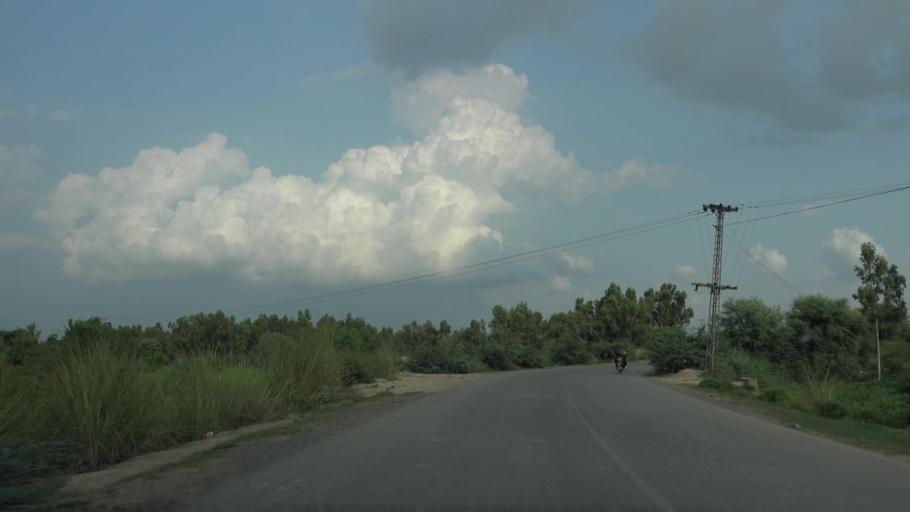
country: PK
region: Punjab
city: Nankana Sahib
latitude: 31.4942
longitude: 73.6026
